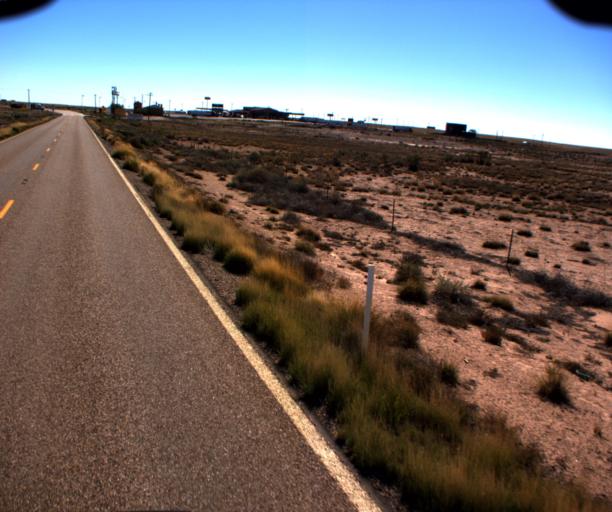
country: US
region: Arizona
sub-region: Navajo County
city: Holbrook
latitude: 34.9792
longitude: -110.0886
